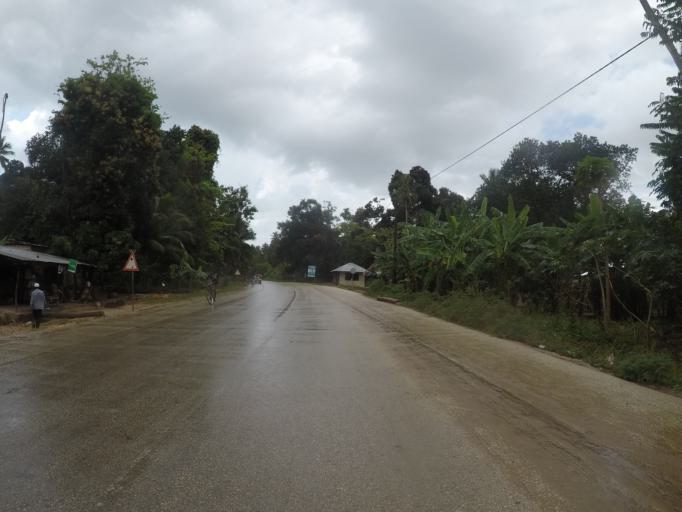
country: TZ
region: Zanzibar North
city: Mkokotoni
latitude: -5.9682
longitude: 39.1967
